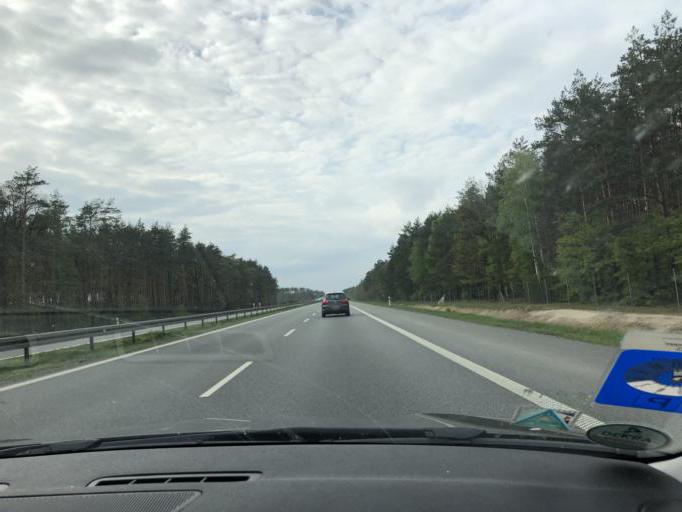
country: PL
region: Opole Voivodeship
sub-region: Powiat opolski
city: Komprachcice
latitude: 50.6110
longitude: 17.7771
